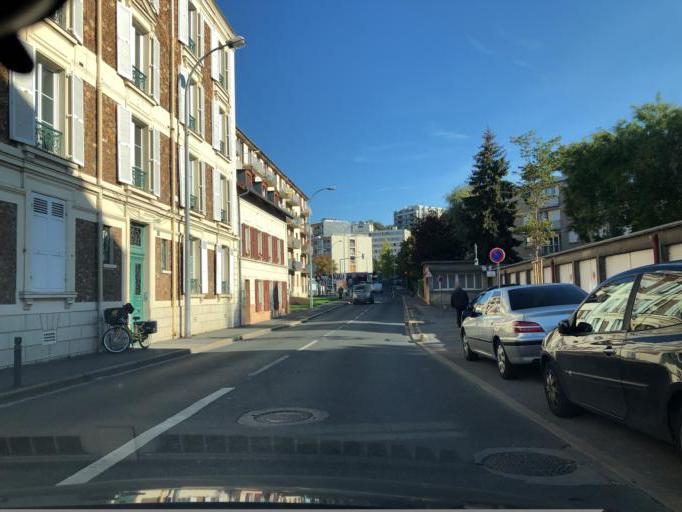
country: FR
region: Ile-de-France
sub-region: Departement des Hauts-de-Seine
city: Chaville
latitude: 48.8008
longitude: 2.1872
